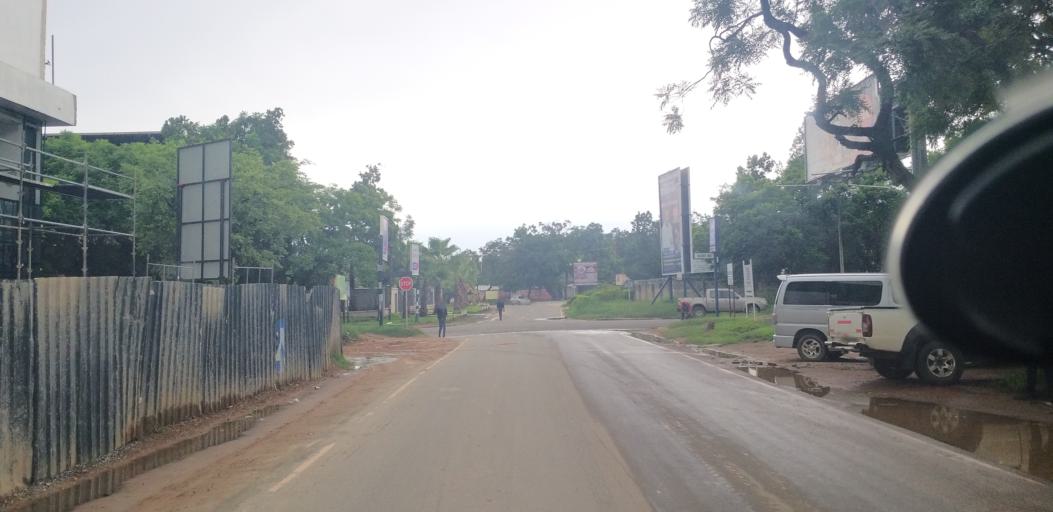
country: ZM
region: Lusaka
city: Lusaka
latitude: -15.4147
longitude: 28.3025
